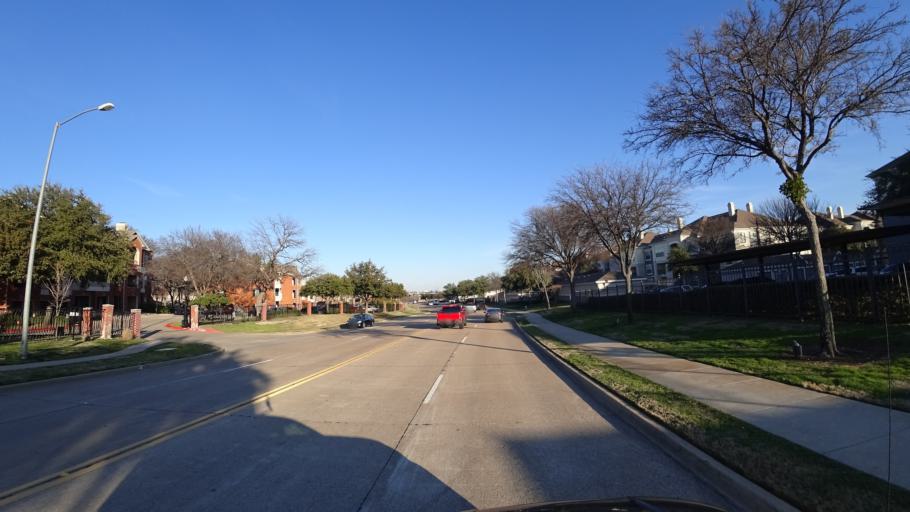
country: US
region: Texas
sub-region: Denton County
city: Lewisville
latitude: 32.9985
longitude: -96.9829
